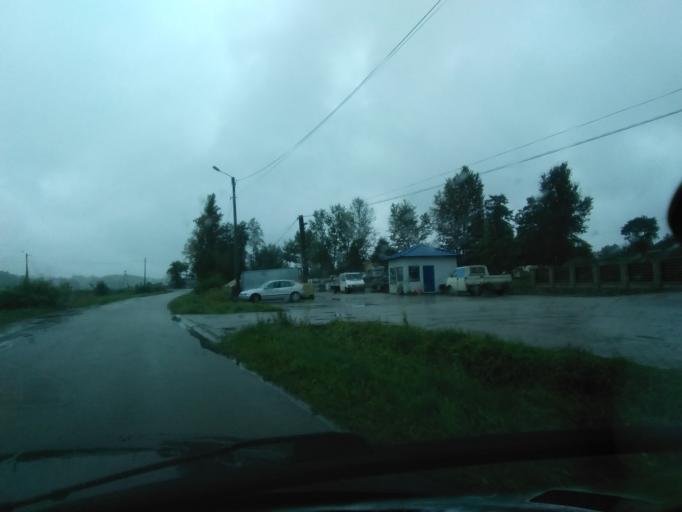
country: PL
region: Subcarpathian Voivodeship
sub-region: Powiat ropczycko-sedziszowski
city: Niedzwiada
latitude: 49.9965
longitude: 21.5546
